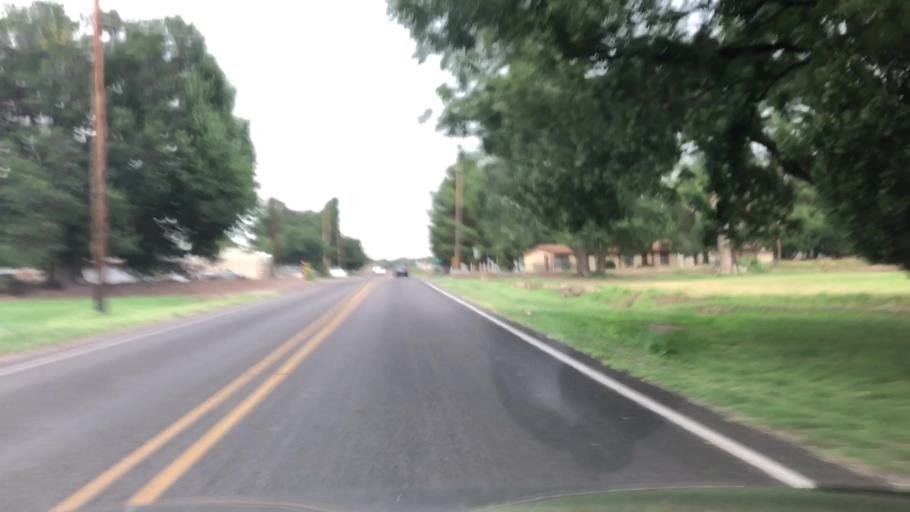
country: US
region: New Mexico
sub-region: Dona Ana County
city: Berino
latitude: 32.0416
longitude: -106.6738
